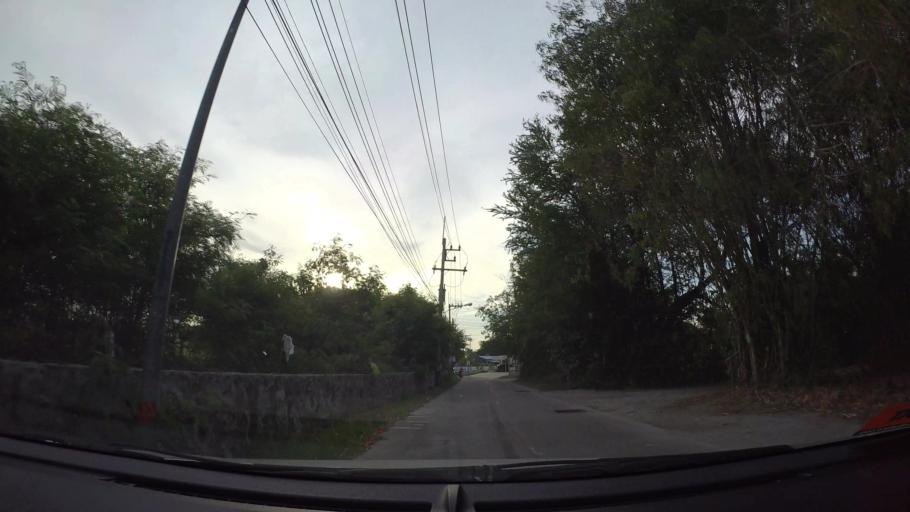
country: TH
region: Chon Buri
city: Chon Buri
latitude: 13.3343
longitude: 100.9839
